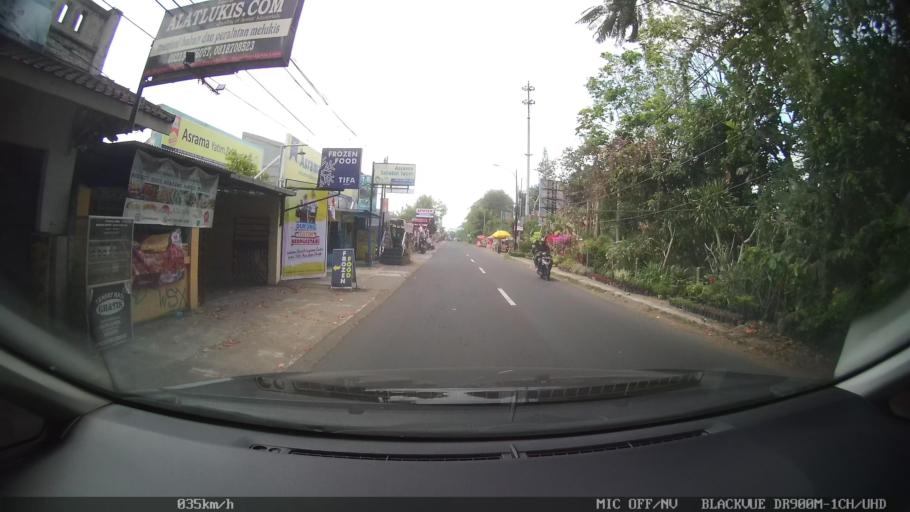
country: ID
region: Daerah Istimewa Yogyakarta
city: Kasihan
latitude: -7.8157
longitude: 110.3487
